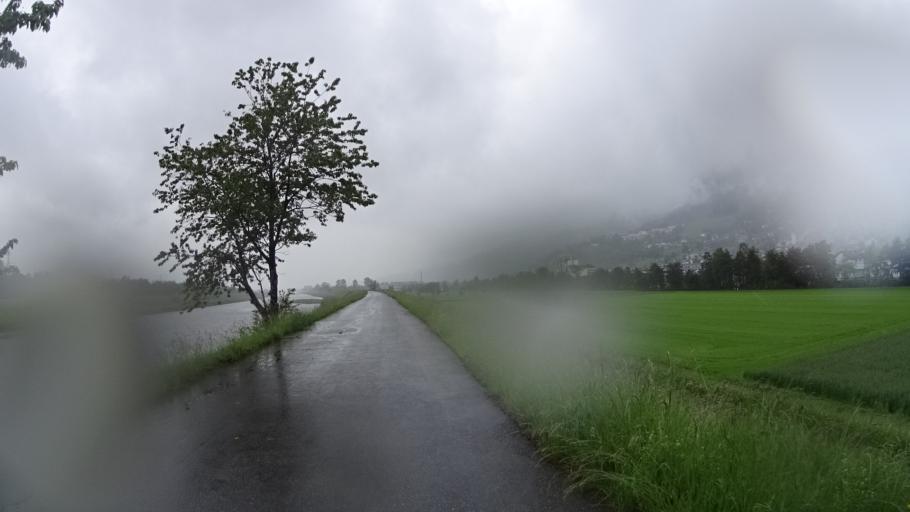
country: LI
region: Triesen
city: Triesen
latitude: 47.0991
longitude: 9.5206
